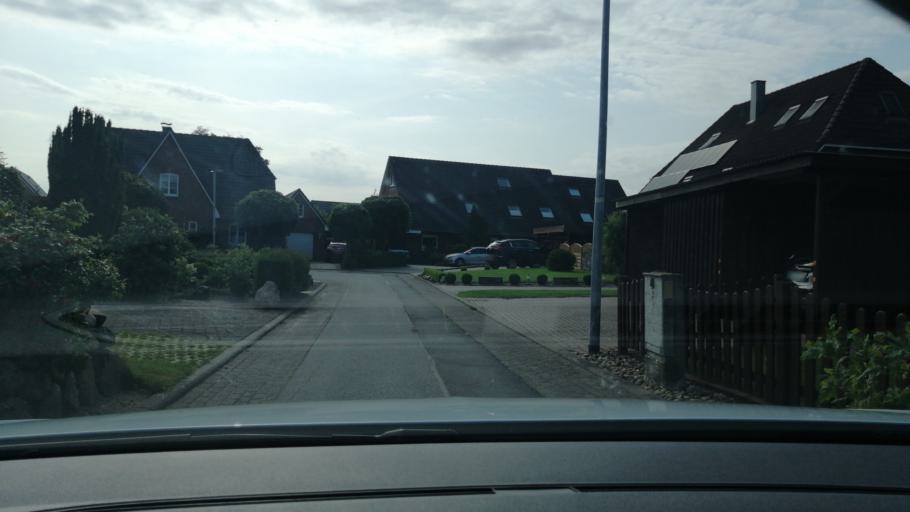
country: DE
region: Schleswig-Holstein
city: Leck
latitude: 54.7765
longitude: 8.9558
